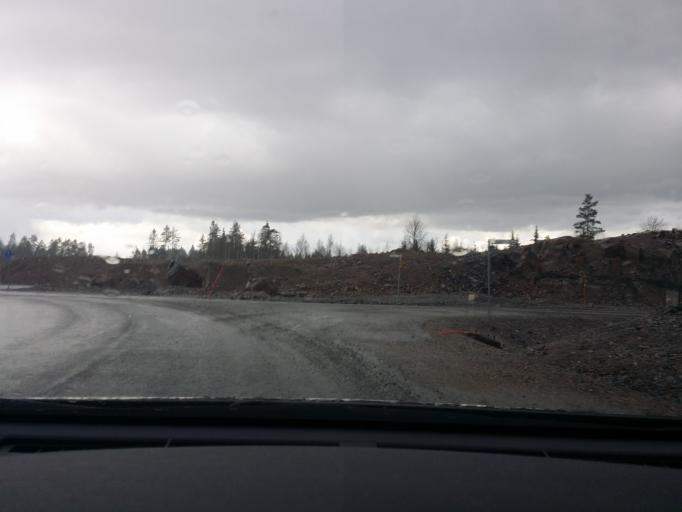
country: SE
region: Soedermanland
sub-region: Eskilstuna Kommun
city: Arla
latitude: 59.3648
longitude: 16.6999
